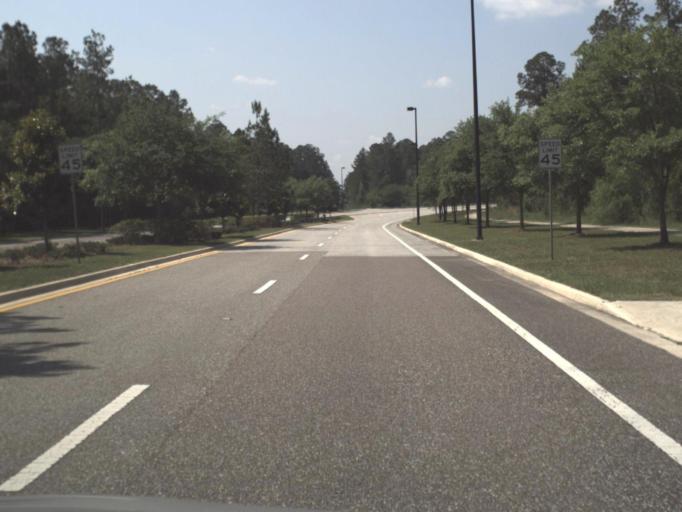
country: US
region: Florida
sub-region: Duval County
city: Baldwin
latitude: 30.2454
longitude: -81.8866
